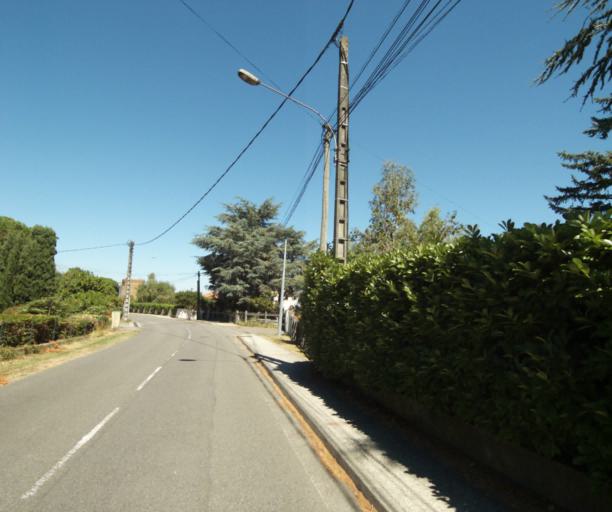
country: FR
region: Midi-Pyrenees
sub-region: Departement de la Haute-Garonne
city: Castanet-Tolosan
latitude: 43.5094
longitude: 1.4980
